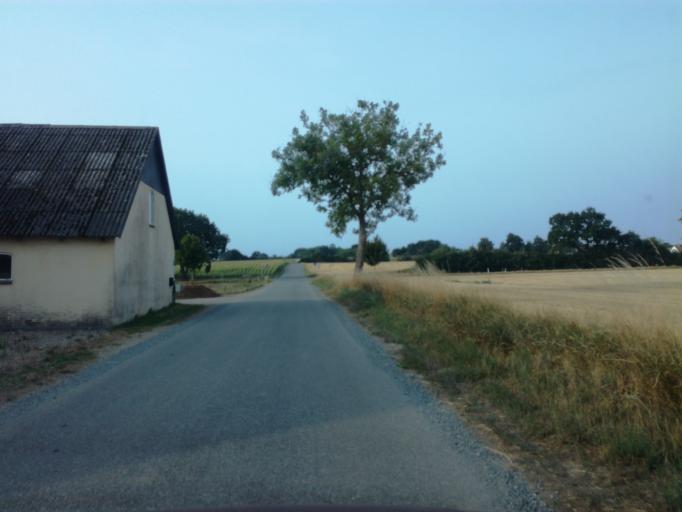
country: DK
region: South Denmark
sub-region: Vejle Kommune
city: Borkop
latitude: 55.6384
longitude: 9.6141
